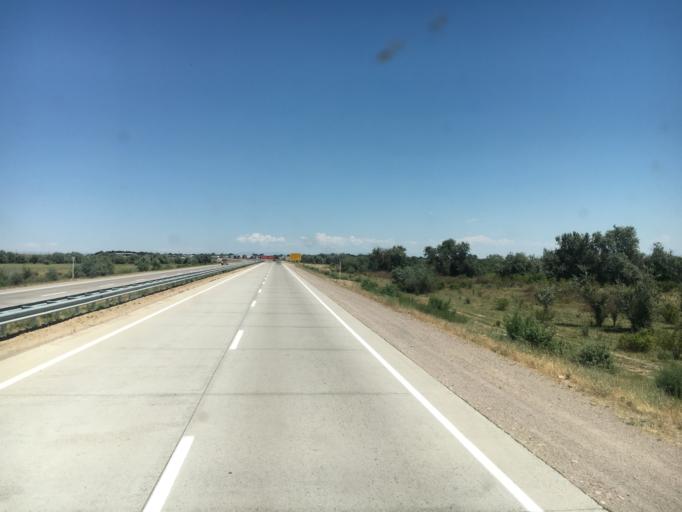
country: KG
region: Chuy
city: Sokuluk
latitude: 43.2678
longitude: 74.2113
